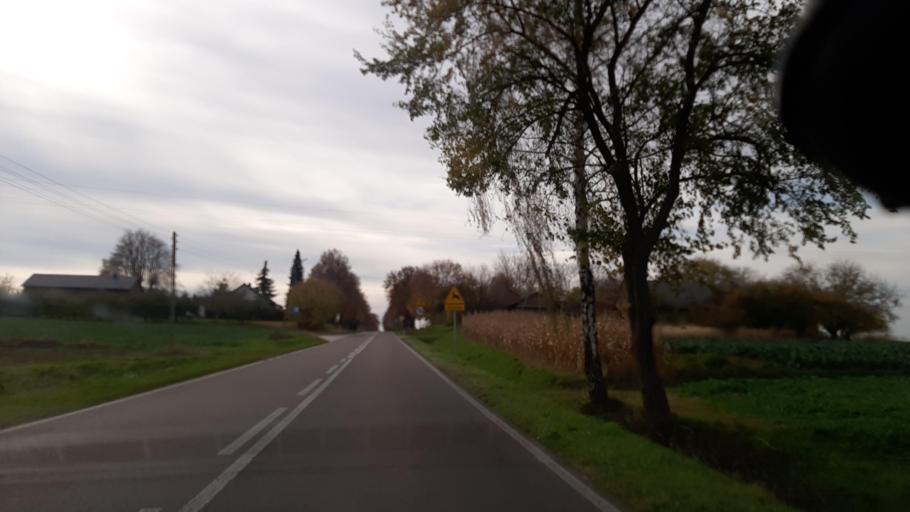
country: PL
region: Lublin Voivodeship
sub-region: Powiat pulawski
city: Markuszow
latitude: 51.3447
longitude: 22.2636
